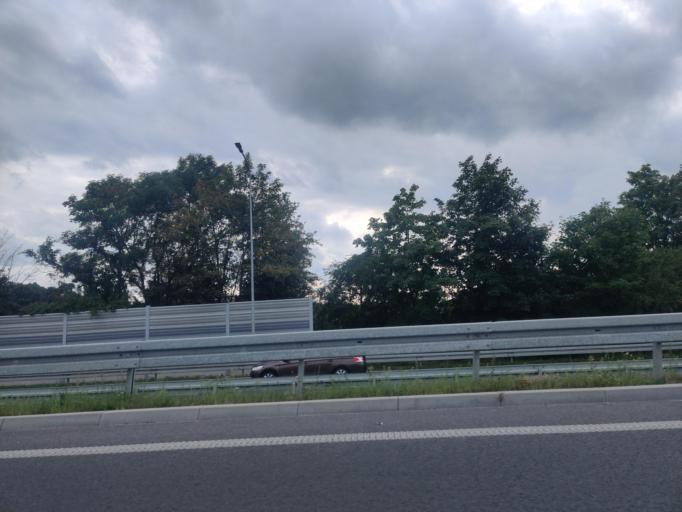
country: PL
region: Greater Poland Voivodeship
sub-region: Konin
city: Konin
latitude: 52.2057
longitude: 18.2682
